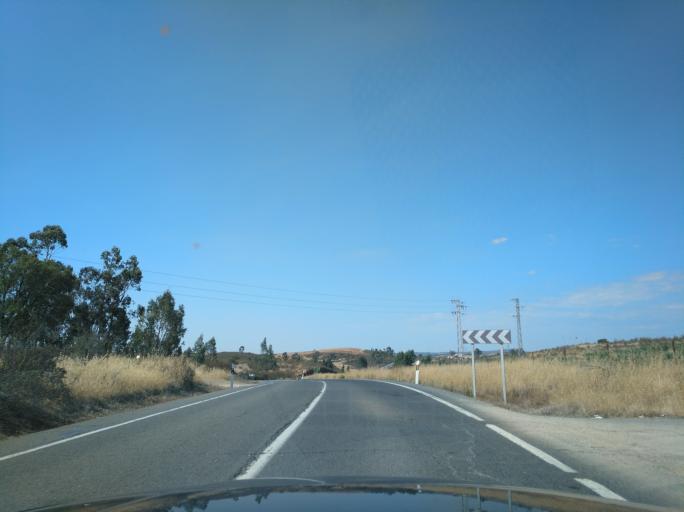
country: ES
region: Andalusia
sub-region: Provincia de Huelva
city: San Bartolome de la Torre
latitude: 37.4881
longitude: -7.1321
